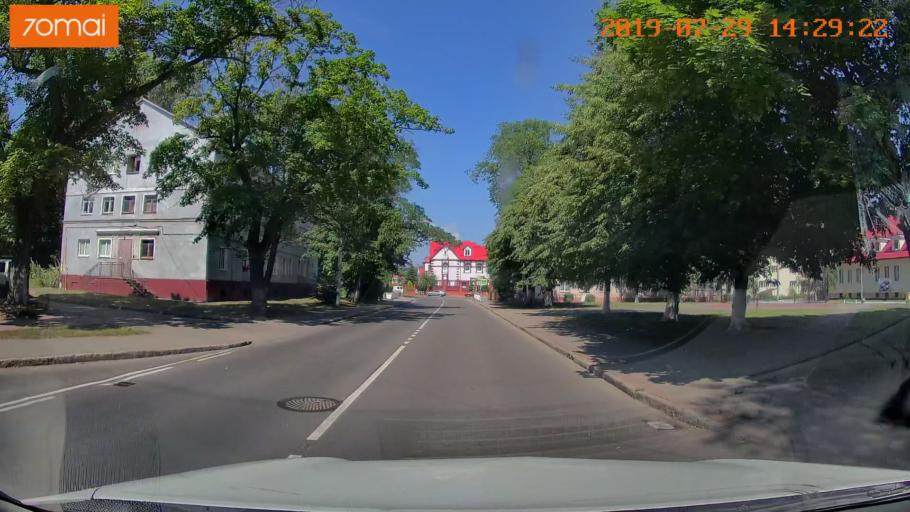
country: RU
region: Kaliningrad
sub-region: Gorod Kaliningrad
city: Baltiysk
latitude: 54.6431
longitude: 19.8919
